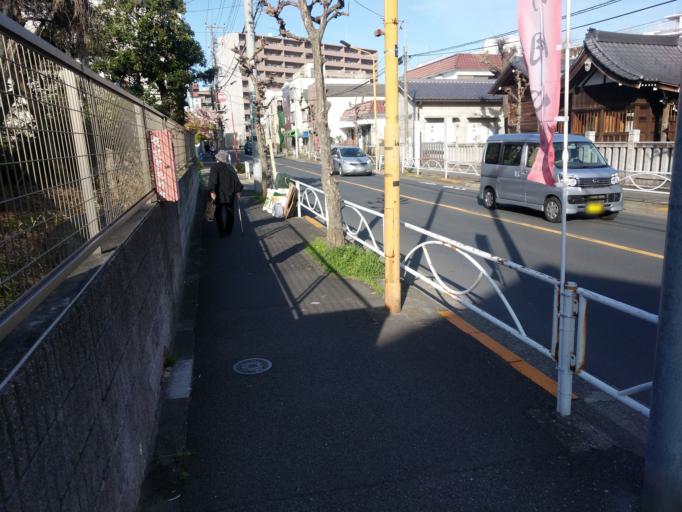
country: JP
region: Tokyo
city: Urayasu
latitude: 35.7091
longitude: 139.8259
